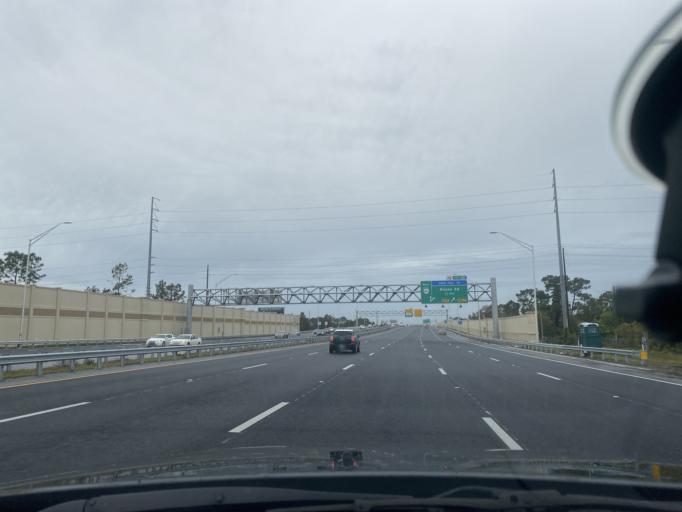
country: US
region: Florida
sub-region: Orange County
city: Alafaya
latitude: 28.5489
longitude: -81.2101
